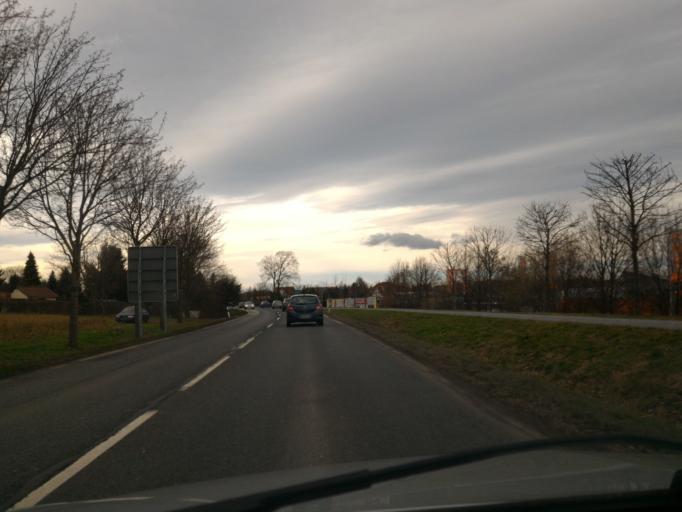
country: DE
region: Saxony
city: Radeberg
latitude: 51.0649
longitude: 13.8930
